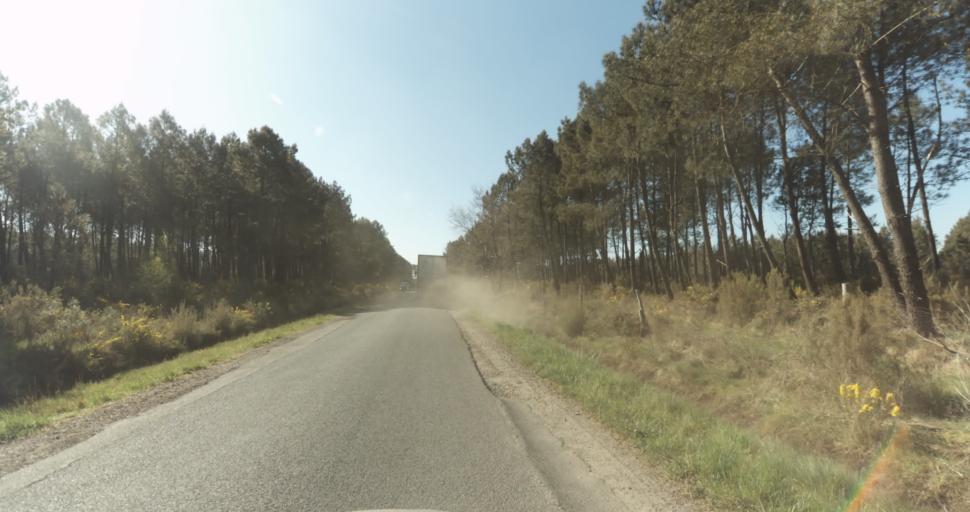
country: FR
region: Aquitaine
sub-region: Departement de la Gironde
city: Marcheprime
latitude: 44.7596
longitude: -0.8521
